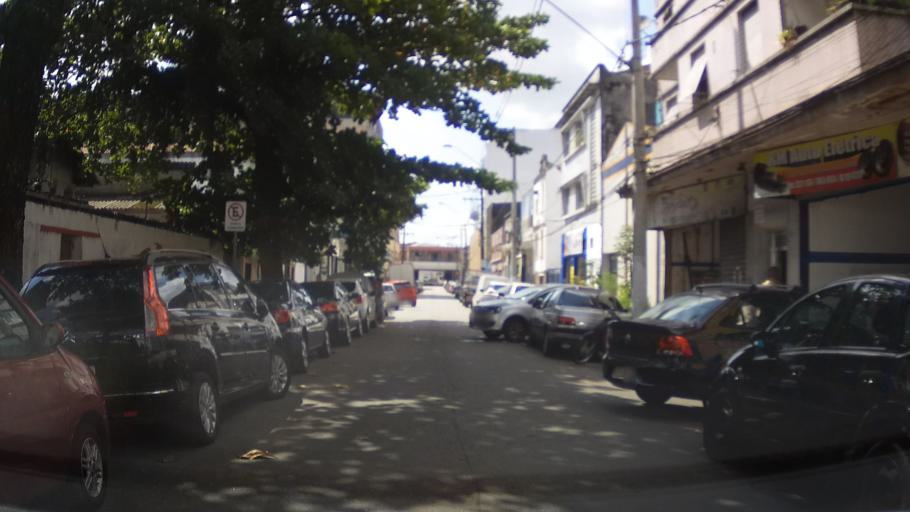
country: BR
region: Sao Paulo
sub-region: Santos
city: Santos
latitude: -23.9431
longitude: -46.3249
